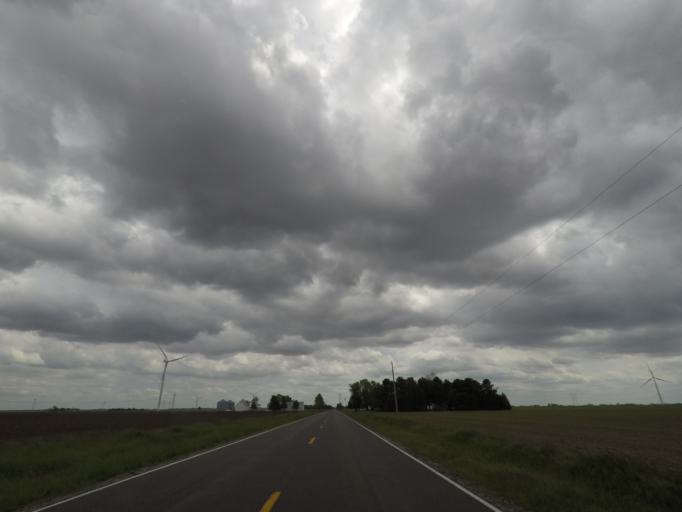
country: US
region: Illinois
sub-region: Macon County
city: Warrensburg
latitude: 40.0043
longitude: -89.0856
